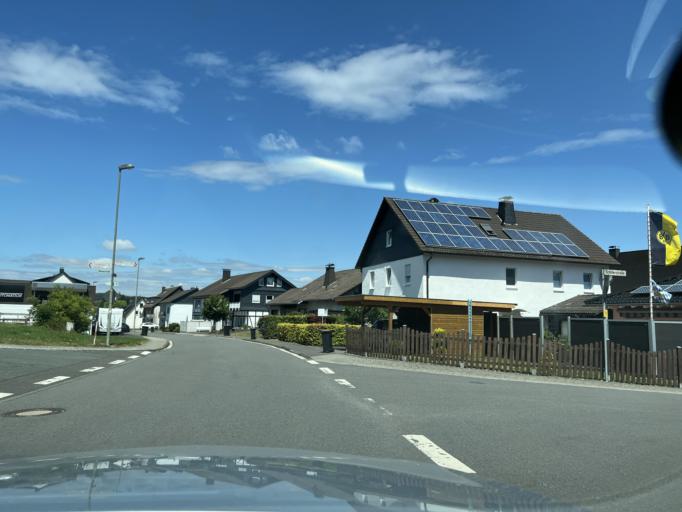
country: DE
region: North Rhine-Westphalia
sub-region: Regierungsbezirk Arnsberg
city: Wenden
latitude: 50.9621
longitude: 7.9011
